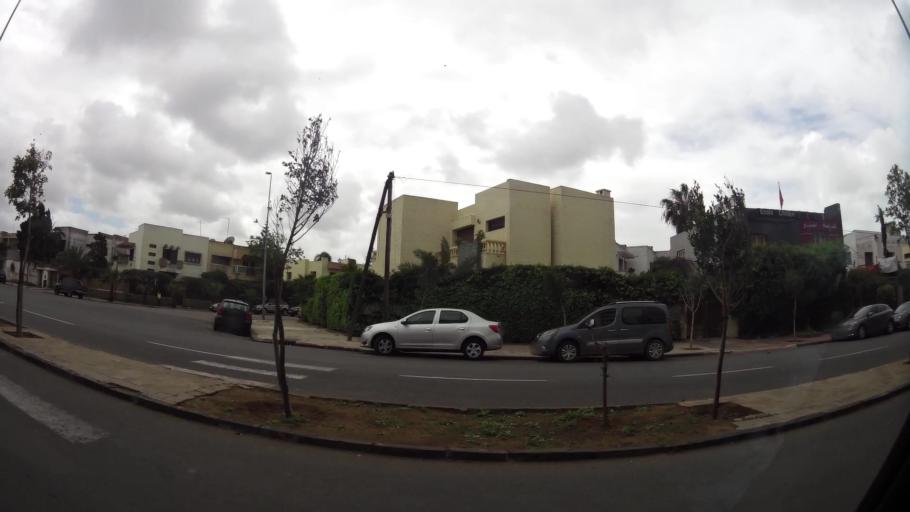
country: MA
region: Grand Casablanca
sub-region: Casablanca
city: Casablanca
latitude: 33.5952
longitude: -7.6462
